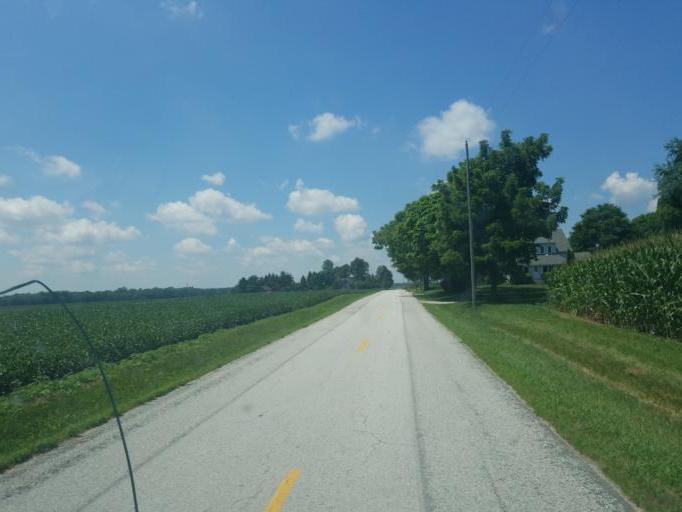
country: US
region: Ohio
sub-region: Allen County
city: Spencerville
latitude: 40.6666
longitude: -84.4266
